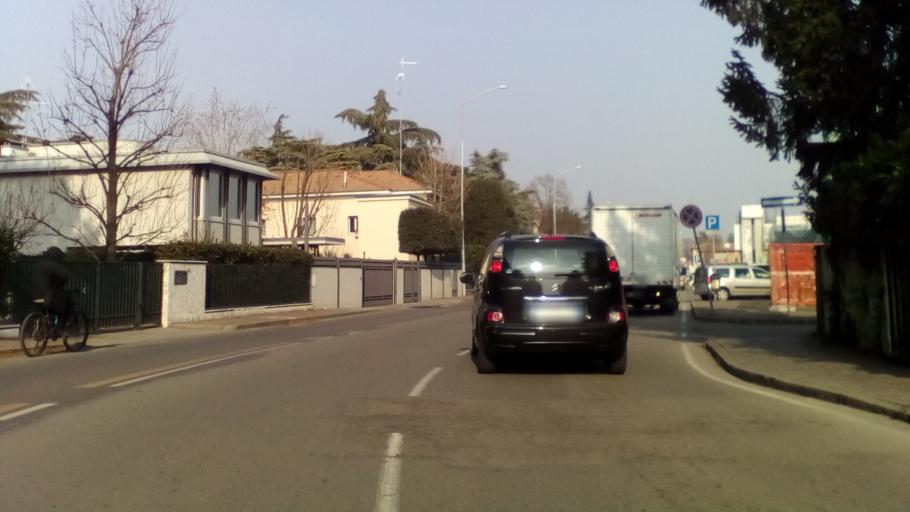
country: IT
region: Emilia-Romagna
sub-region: Provincia di Modena
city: Modena
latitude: 44.6347
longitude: 10.9374
